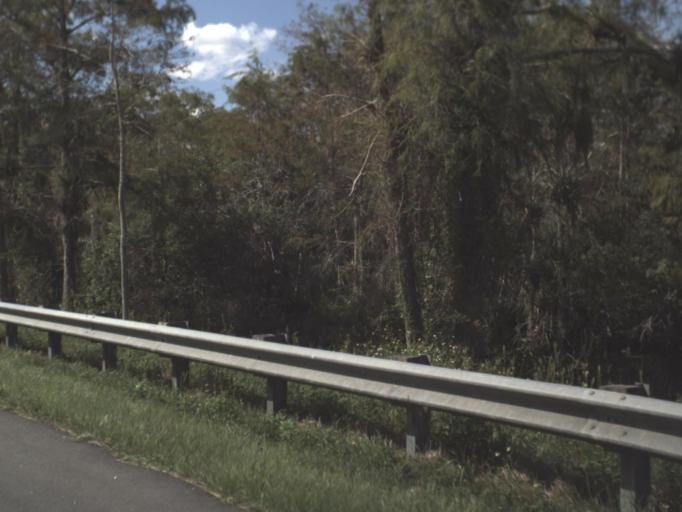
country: US
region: Florida
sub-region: Miami-Dade County
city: Kendall West
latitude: 25.8492
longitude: -80.9571
